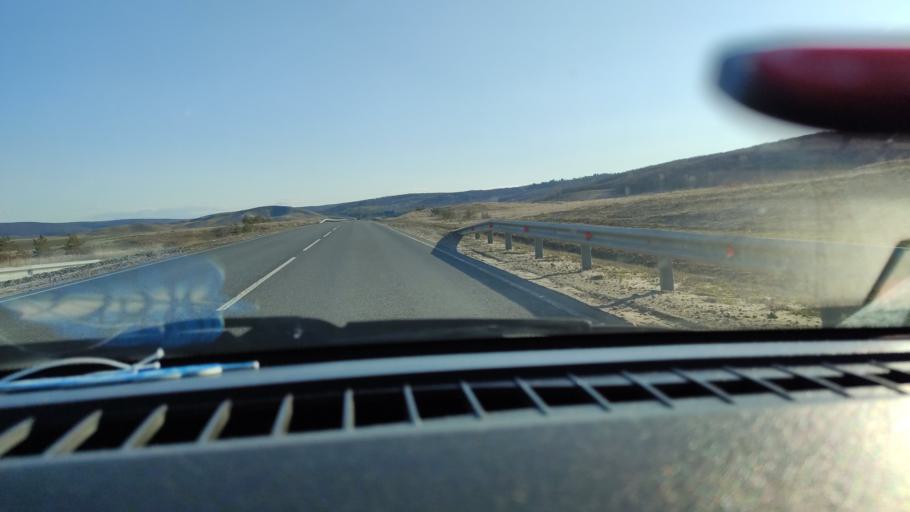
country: RU
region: Saratov
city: Alekseyevka
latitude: 52.3573
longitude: 47.9490
